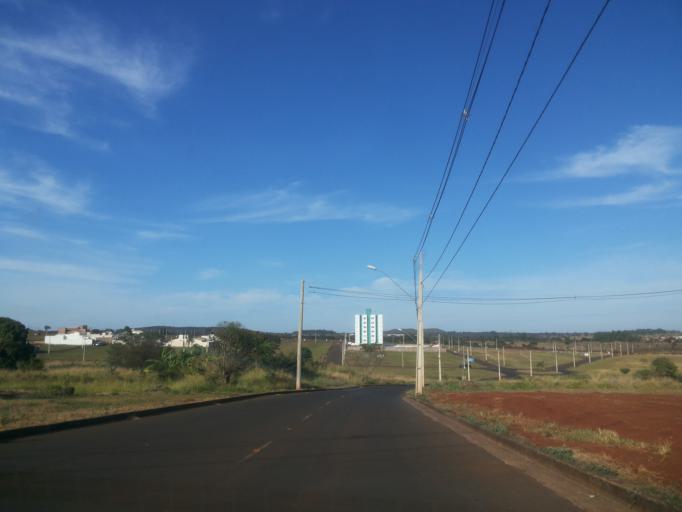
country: BR
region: Minas Gerais
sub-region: Ituiutaba
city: Ituiutaba
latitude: -18.9963
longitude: -49.4665
